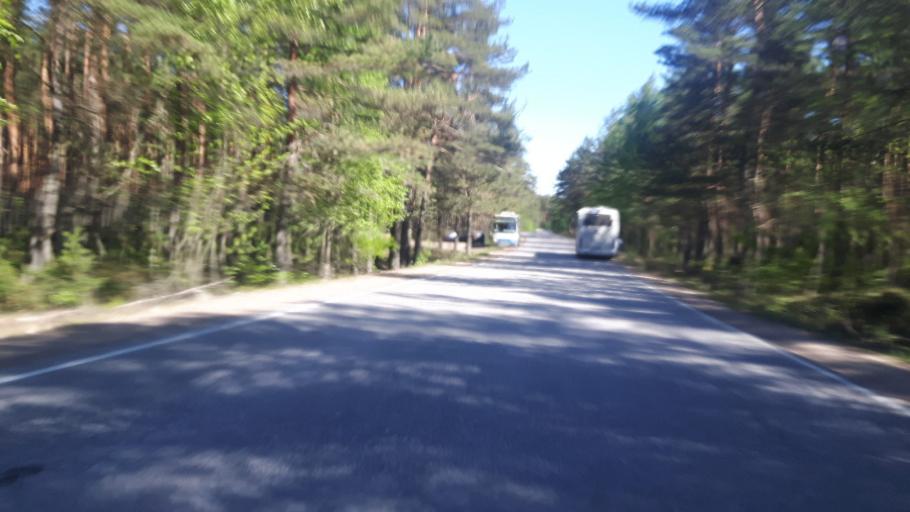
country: RU
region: Leningrad
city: Glebychevo
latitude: 60.2777
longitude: 28.8999
